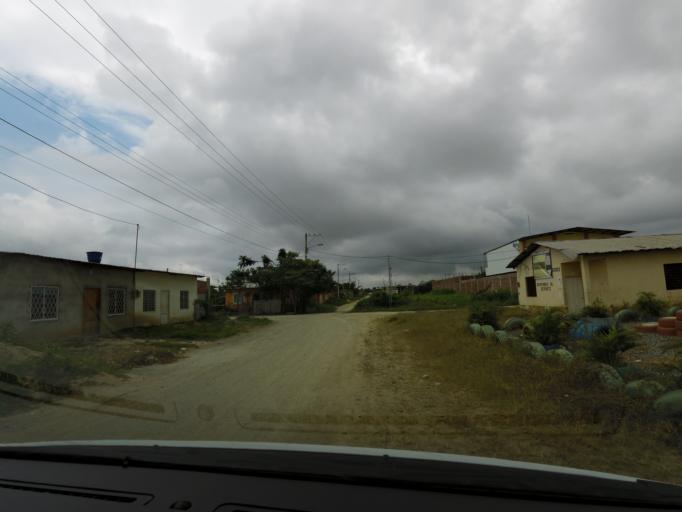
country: EC
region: El Oro
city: Huaquillas
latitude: -3.4857
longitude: -80.2086
